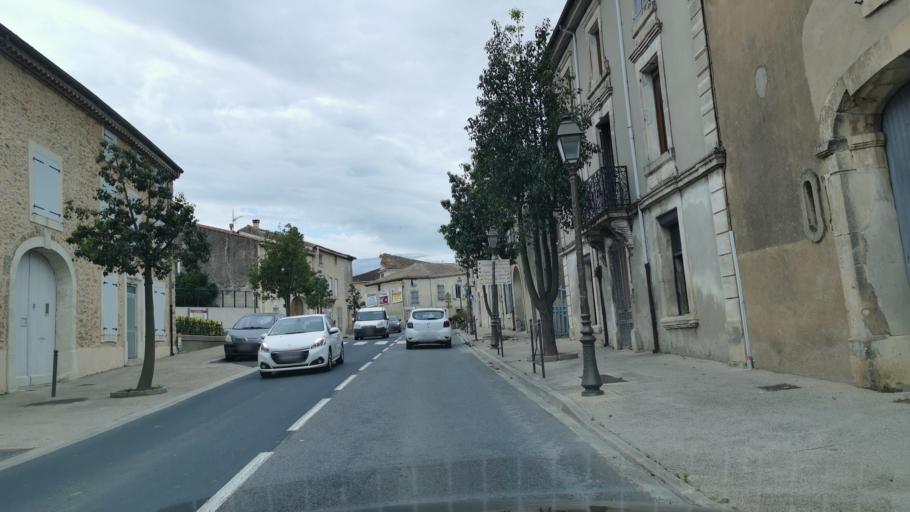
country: FR
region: Languedoc-Roussillon
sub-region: Departement de l'Aude
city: Marcorignan
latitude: 43.2267
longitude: 2.9223
